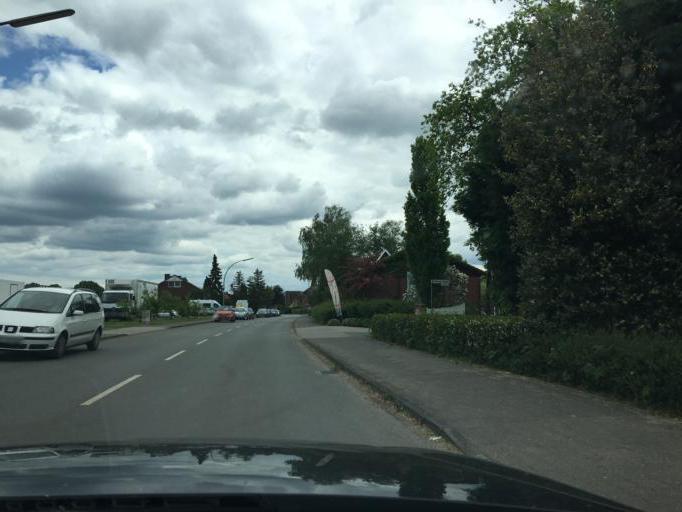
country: DE
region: North Rhine-Westphalia
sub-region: Regierungsbezirk Munster
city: Muenster
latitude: 52.0326
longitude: 7.6741
